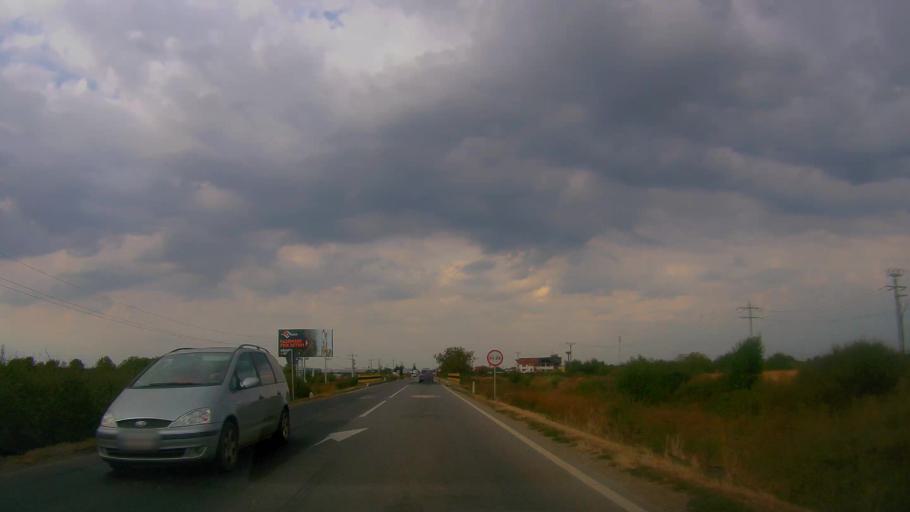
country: RO
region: Satu Mare
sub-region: Comuna Paulesti
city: Paulesti
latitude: 47.8118
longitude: 22.9229
